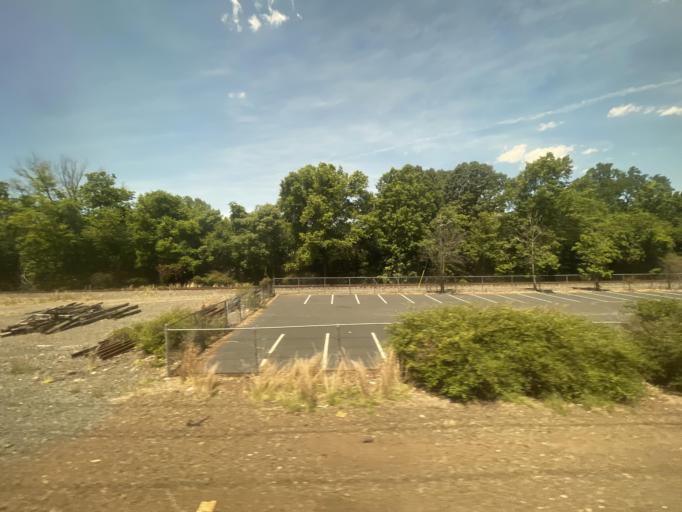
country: US
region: New Jersey
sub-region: Middlesex County
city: New Brunswick
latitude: 40.4755
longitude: -74.4690
